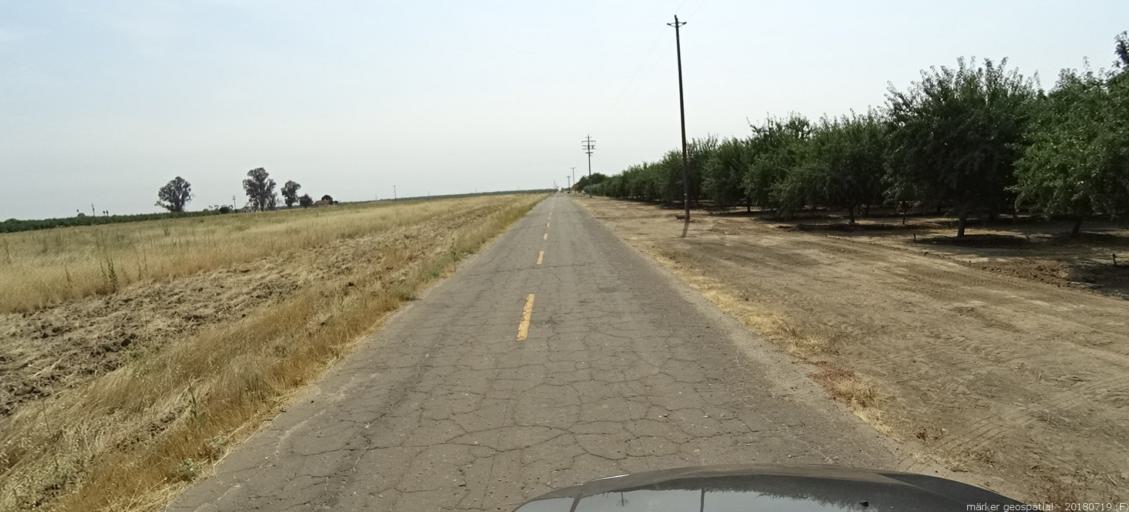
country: US
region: California
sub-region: Madera County
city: Fairmead
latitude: 37.0837
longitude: -120.1878
